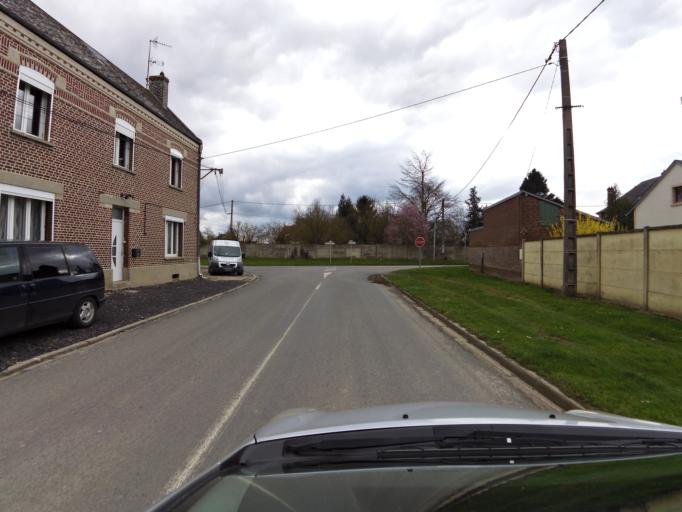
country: FR
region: Picardie
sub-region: Departement de la Somme
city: Roye
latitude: 49.7380
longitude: 2.7775
